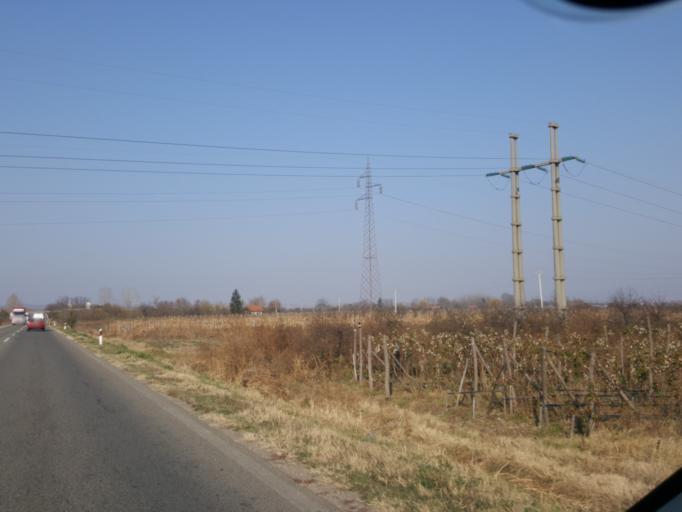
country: RS
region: Central Serbia
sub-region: Jablanicki Okrug
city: Leskovac
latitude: 43.0155
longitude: 21.9554
